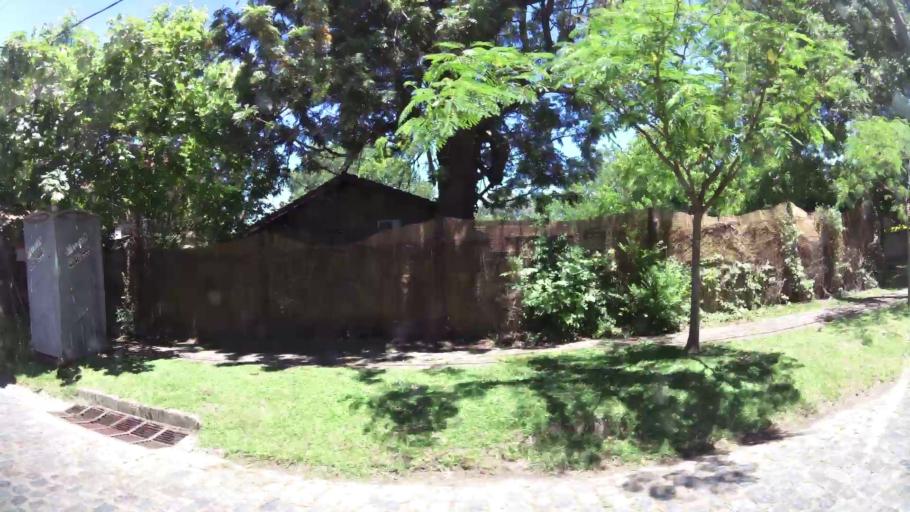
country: AR
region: Buenos Aires
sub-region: Partido de San Isidro
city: San Isidro
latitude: -34.4969
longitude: -58.5636
